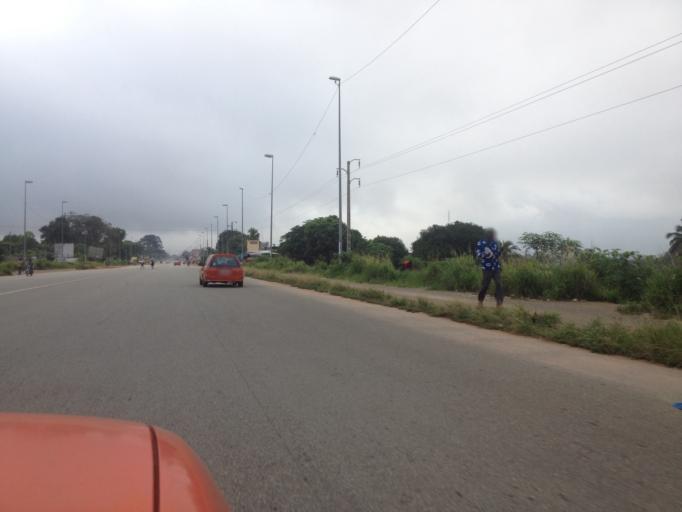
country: CI
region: Vallee du Bandama
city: Bouake
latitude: 7.6866
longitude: -5.0556
